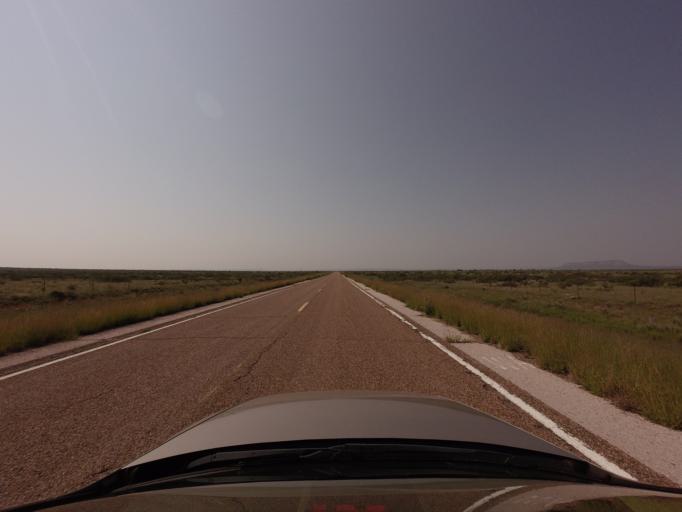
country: US
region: New Mexico
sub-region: Quay County
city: Tucumcari
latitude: 34.9872
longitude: -103.7480
